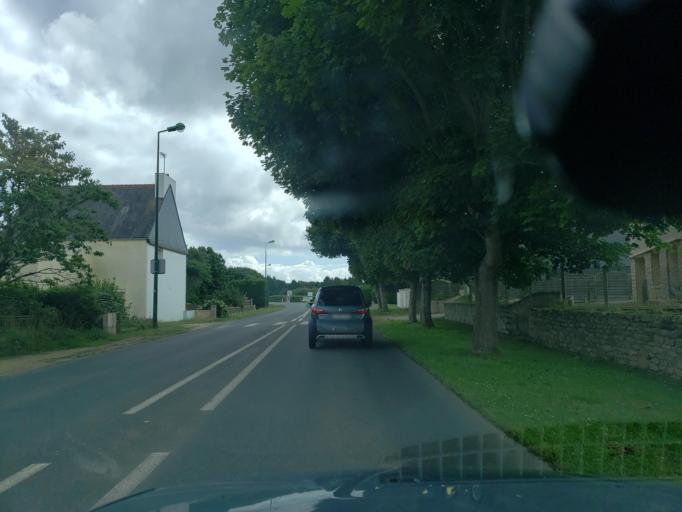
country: FR
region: Brittany
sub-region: Departement du Finistere
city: Plomeur
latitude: 47.8609
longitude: -4.2812
